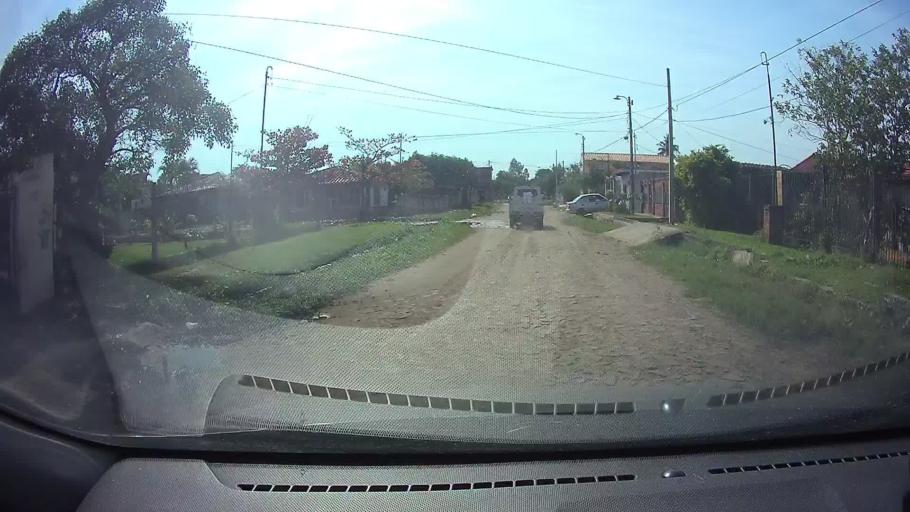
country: PY
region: Central
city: Colonia Mariano Roque Alonso
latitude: -25.2221
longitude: -57.5234
